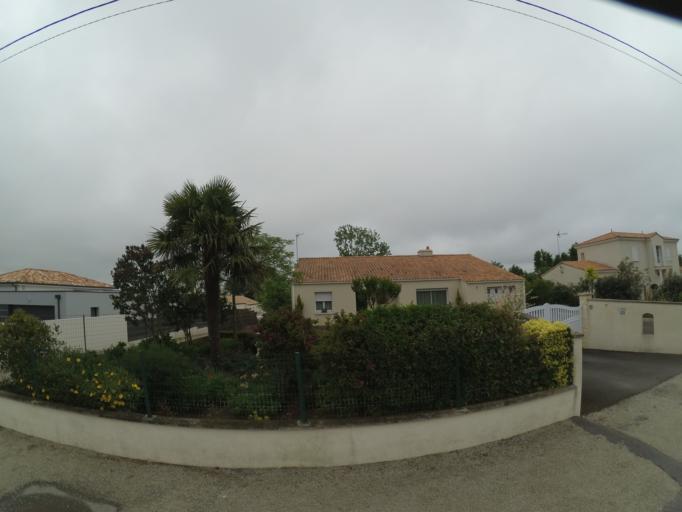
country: FR
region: Pays de la Loire
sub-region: Departement de la Vendee
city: La Roche-sur-Yon
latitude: 46.6426
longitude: -1.4334
